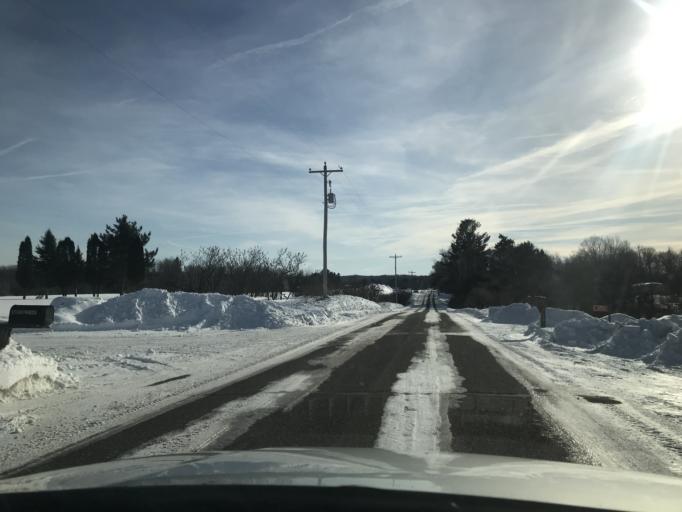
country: US
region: Wisconsin
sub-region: Menominee County
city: Legend Lake
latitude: 45.3141
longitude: -88.5216
